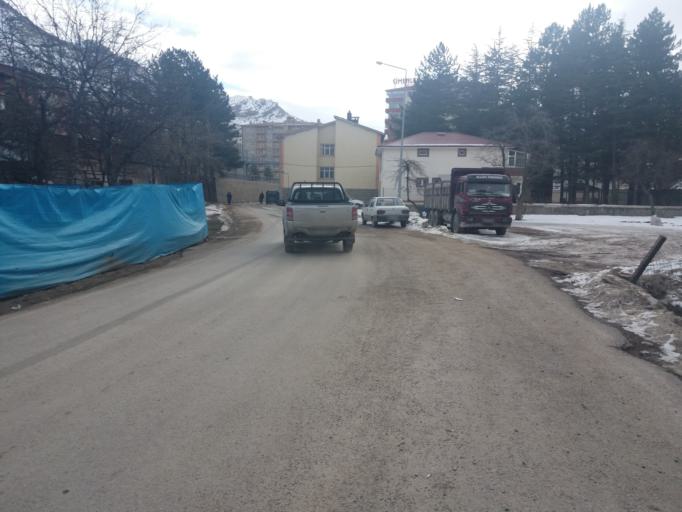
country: TR
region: Gumushane
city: Gumushkhane
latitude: 40.4515
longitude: 39.4937
